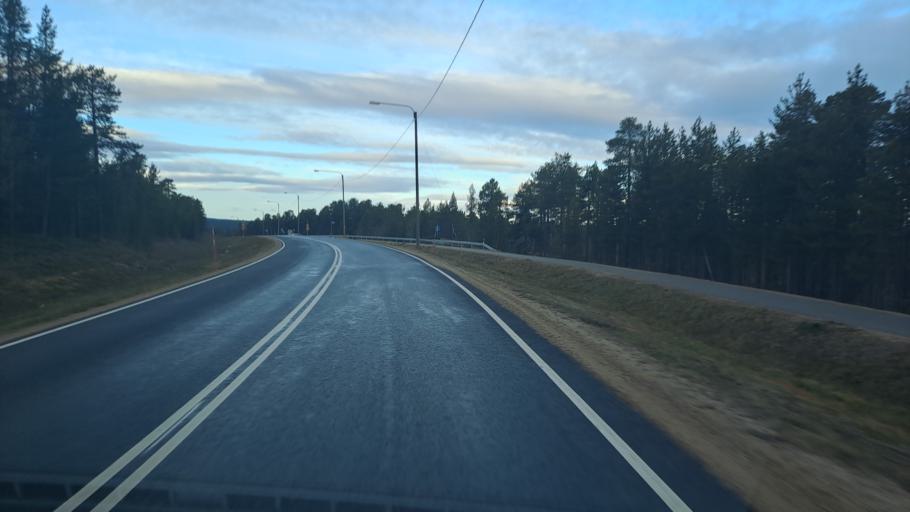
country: FI
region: Lapland
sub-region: Pohjois-Lappi
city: Inari
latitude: 68.9005
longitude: 27.0762
